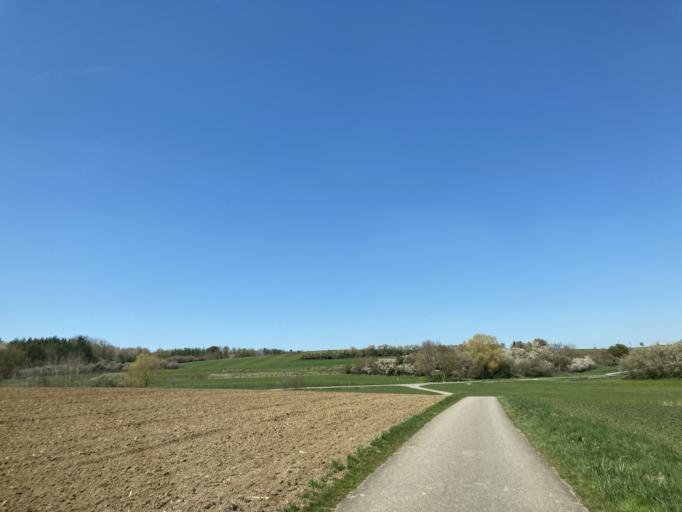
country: DE
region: Baden-Wuerttemberg
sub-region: Tuebingen Region
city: Rottenburg
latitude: 48.4866
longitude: 8.9045
